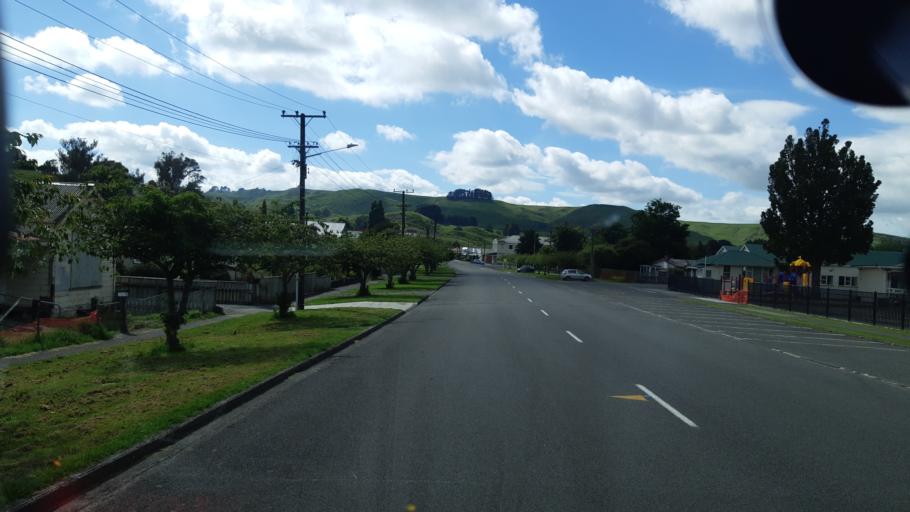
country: NZ
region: Manawatu-Wanganui
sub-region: Rangitikei District
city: Bulls
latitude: -39.9346
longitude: 175.5644
